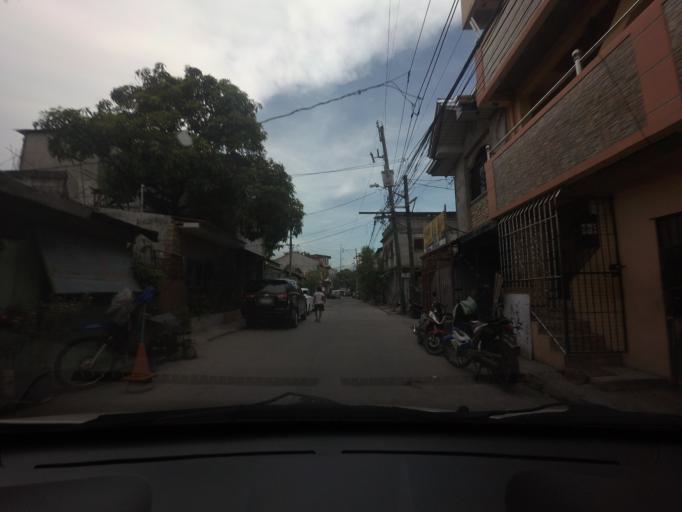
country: PH
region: Calabarzon
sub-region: Province of Rizal
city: Taguig
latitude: 14.5226
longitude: 121.0598
